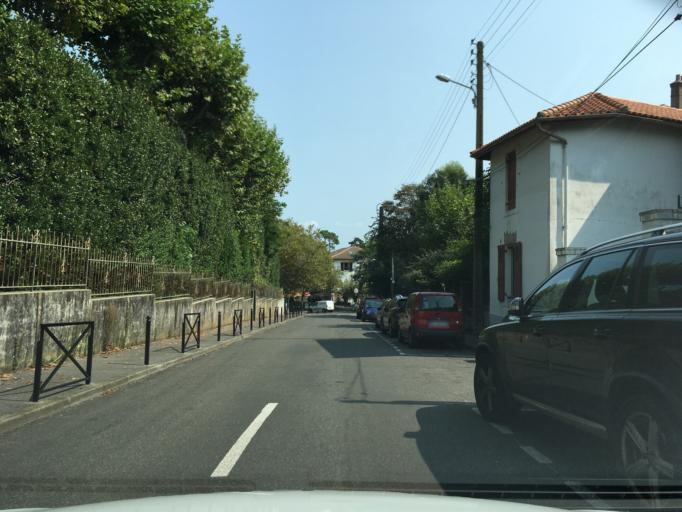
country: FR
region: Aquitaine
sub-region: Departement des Pyrenees-Atlantiques
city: Biarritz
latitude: 43.4967
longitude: -1.5400
